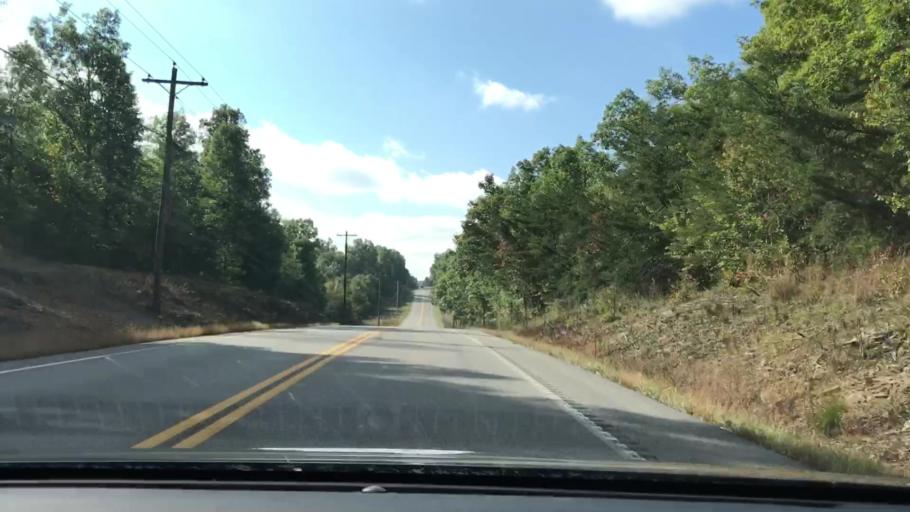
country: US
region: Tennessee
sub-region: Putnam County
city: Monterey
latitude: 36.1329
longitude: -85.2136
